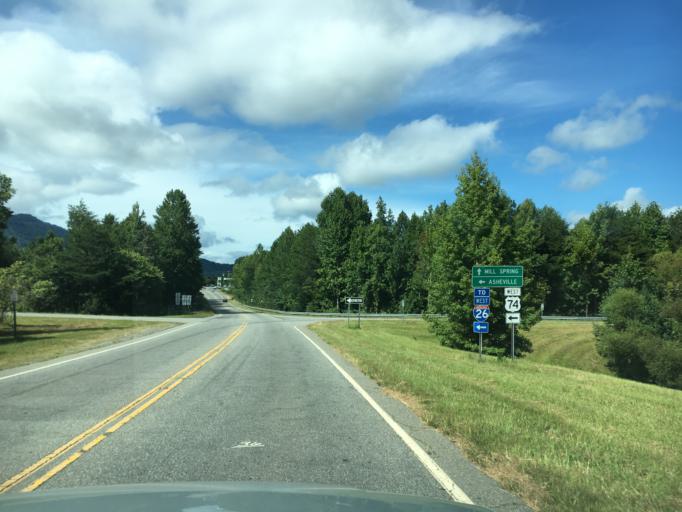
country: US
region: North Carolina
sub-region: Polk County
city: Columbus
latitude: 35.2596
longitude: -82.1826
